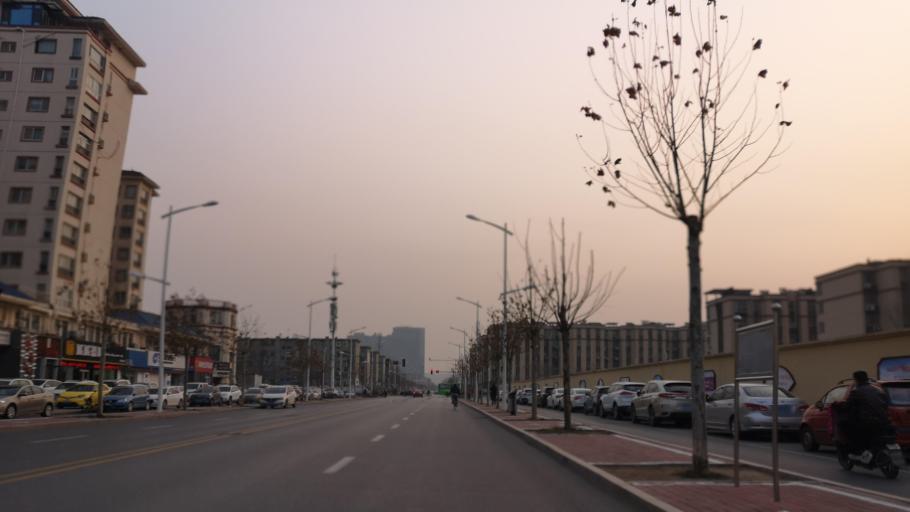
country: CN
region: Henan Sheng
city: Zhongyuanlu
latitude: 35.7850
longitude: 115.0813
